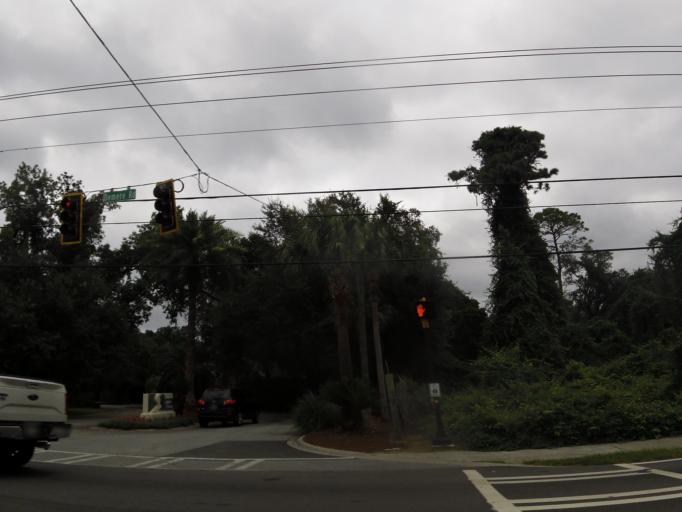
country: US
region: Georgia
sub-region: Glynn County
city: Saint Simon Mills
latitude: 31.1613
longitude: -81.3942
